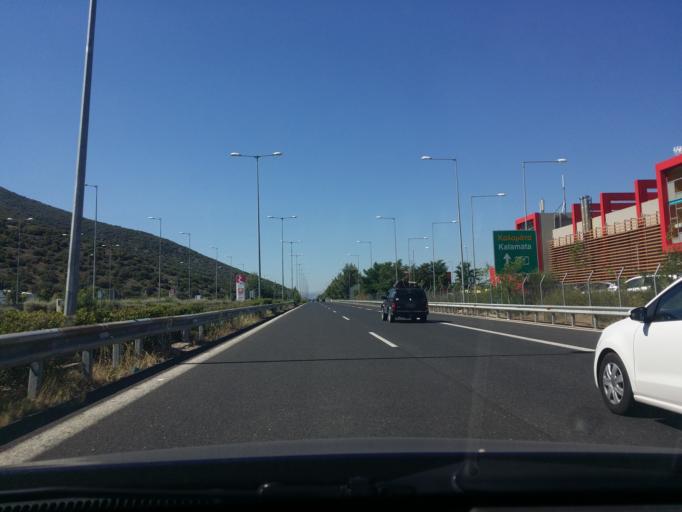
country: GR
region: Peloponnese
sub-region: Nomos Arkadias
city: Tripoli
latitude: 37.5806
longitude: 22.4317
